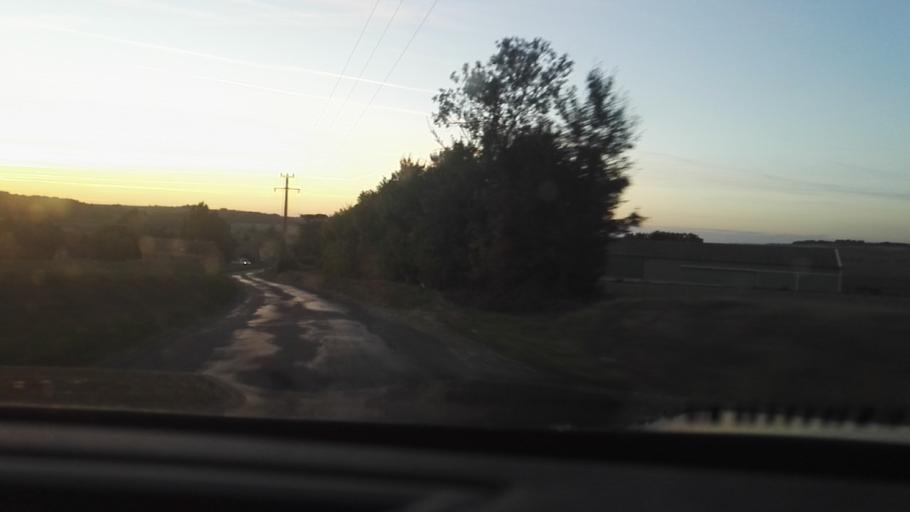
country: FR
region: Haute-Normandie
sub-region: Departement de l'Eure
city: Breuilpont
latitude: 48.9778
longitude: 1.4287
